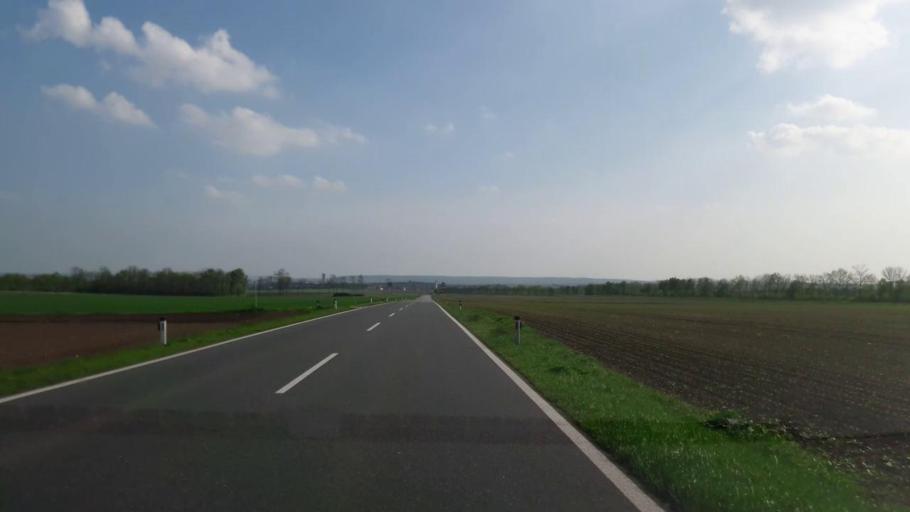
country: AT
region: Lower Austria
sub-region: Politischer Bezirk Hollabrunn
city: Guntersdorf
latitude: 48.6713
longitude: 16.0538
